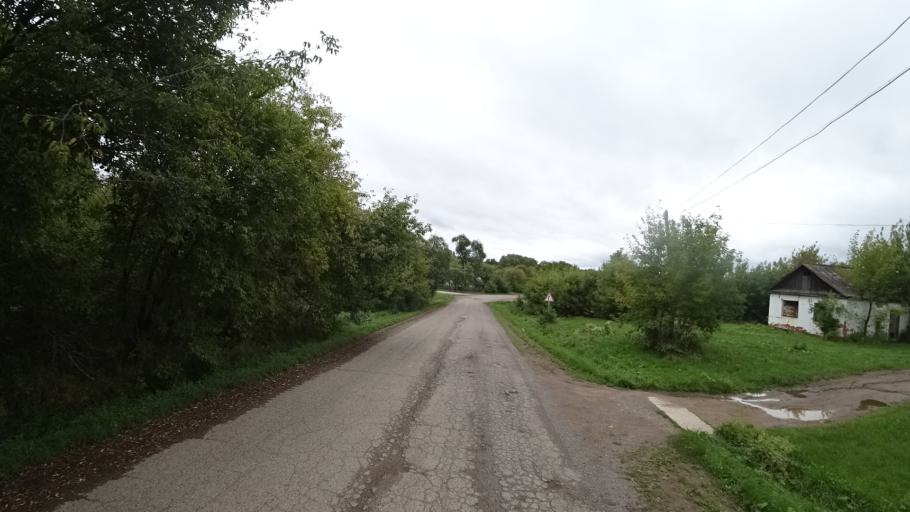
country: RU
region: Primorskiy
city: Chernigovka
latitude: 44.4617
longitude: 132.5915
